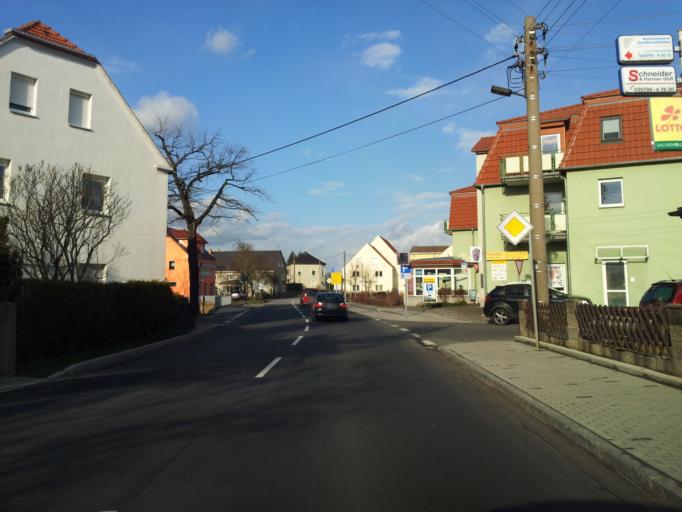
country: DE
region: Saxony
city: Laussnitz
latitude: 51.2470
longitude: 13.8768
